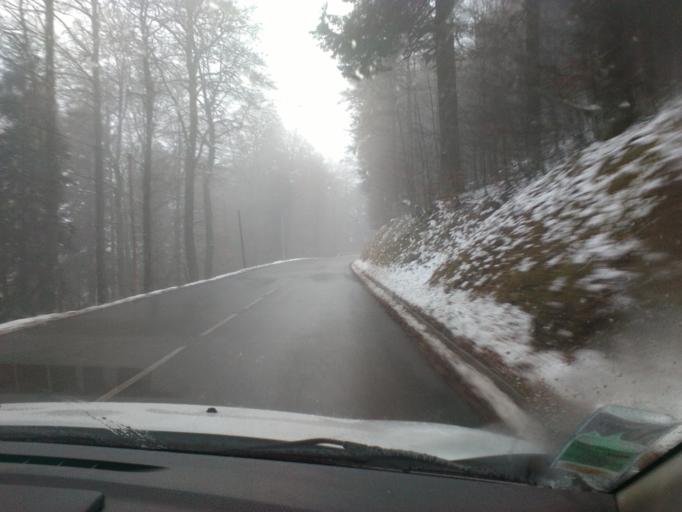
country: FR
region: Lorraine
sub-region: Departement des Vosges
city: Xonrupt-Longemer
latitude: 48.0638
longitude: 6.9945
